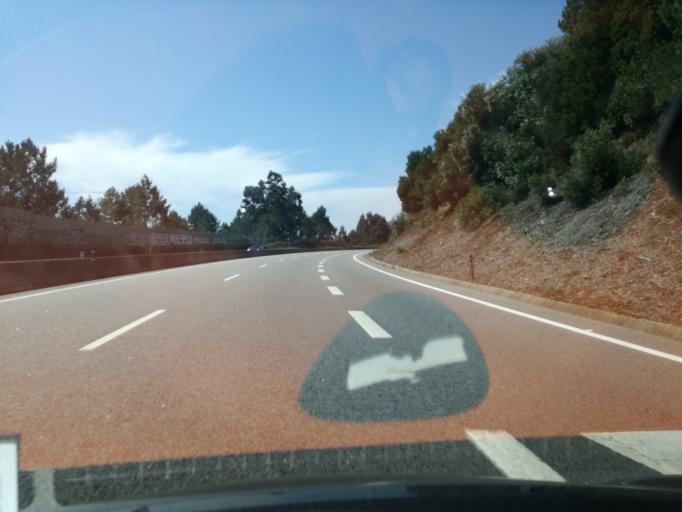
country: PT
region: Viana do Castelo
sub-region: Viana do Castelo
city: Meadela
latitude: 41.7724
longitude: -8.7823
